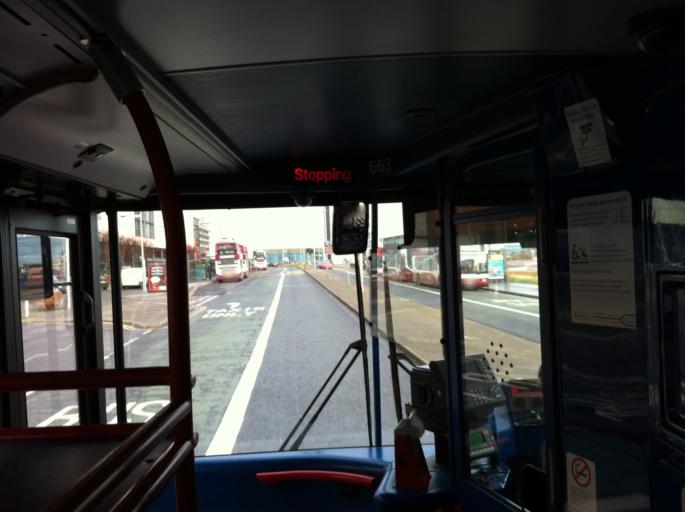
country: GB
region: Scotland
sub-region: Edinburgh
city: Edinburgh
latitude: 55.9789
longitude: -3.1798
